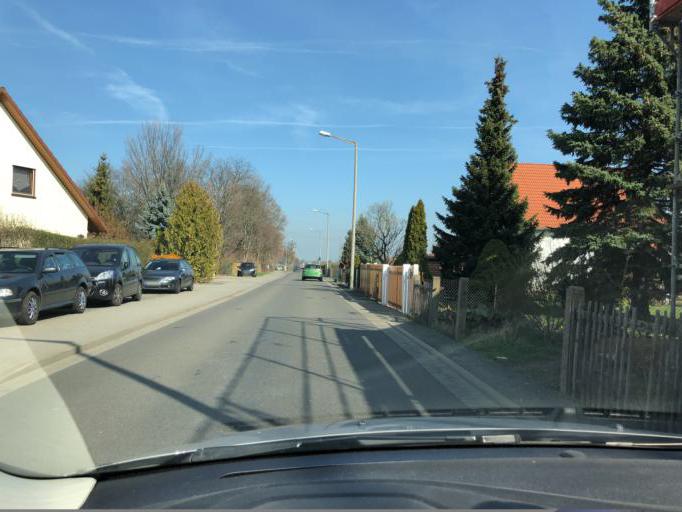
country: DE
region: Saxony
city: Rackwitz
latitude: 51.4070
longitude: 12.4188
